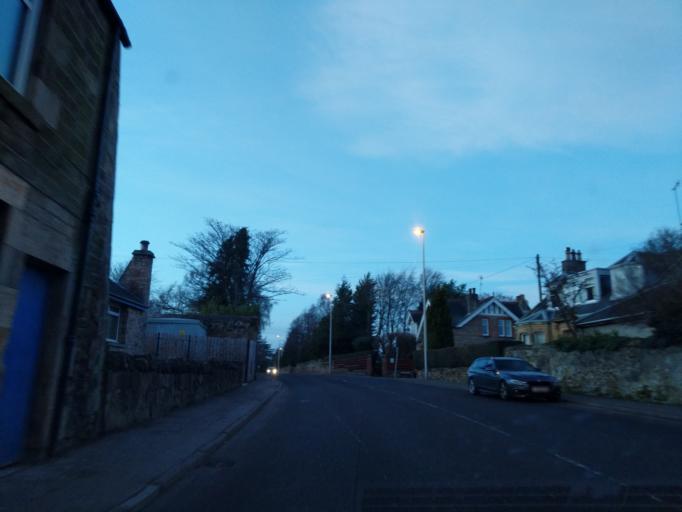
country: GB
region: Scotland
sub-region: Midlothian
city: Bonnyrigg
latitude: 55.8794
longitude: -3.1085
